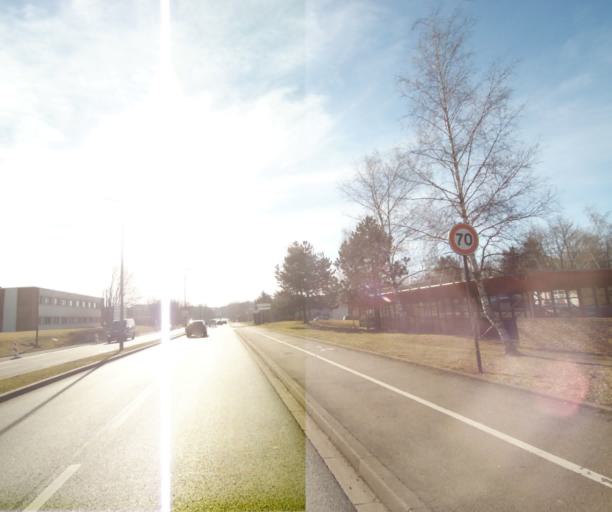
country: FR
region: Lorraine
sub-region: Departement de Meurthe-et-Moselle
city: Villers-les-Nancy
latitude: 48.6561
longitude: 6.1321
